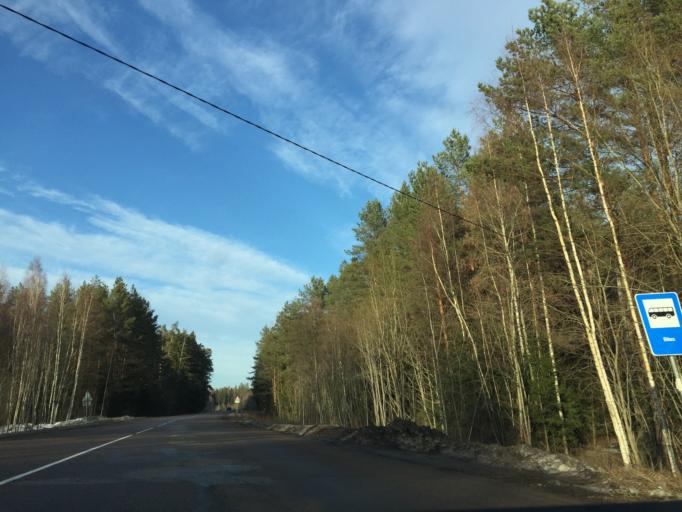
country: LV
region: Kekava
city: Balozi
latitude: 56.7511
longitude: 24.1074
